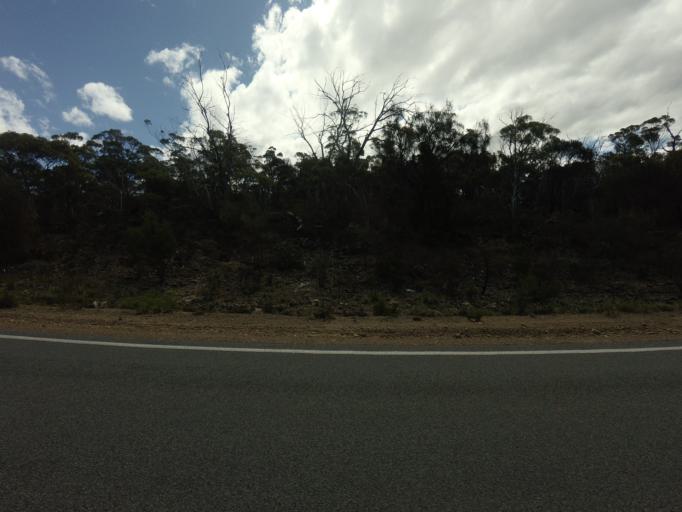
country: AU
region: Tasmania
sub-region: Break O'Day
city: St Helens
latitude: -42.0158
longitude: 147.9761
